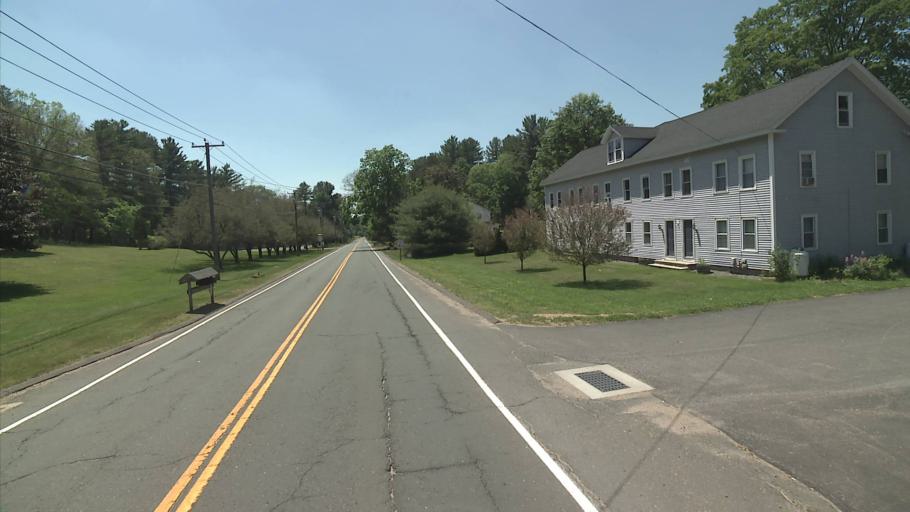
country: US
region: Connecticut
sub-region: Tolland County
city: Stafford
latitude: 41.9924
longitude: -72.2788
